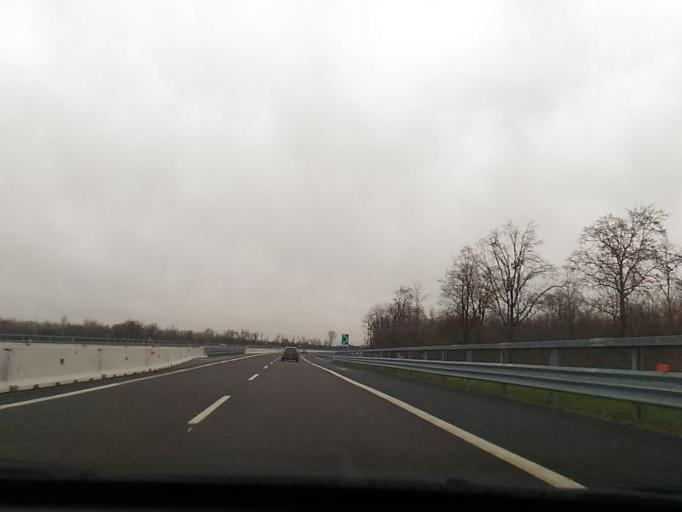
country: IT
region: Lombardy
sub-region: Provincia di Como
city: Carbonate
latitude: 45.6617
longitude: 8.9319
